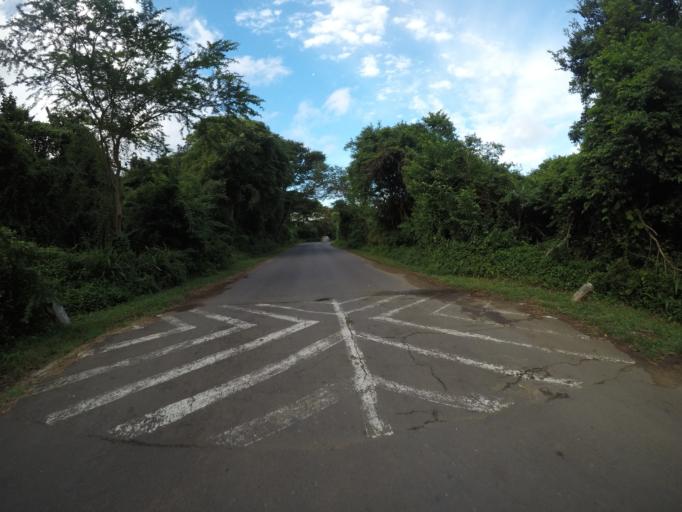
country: ZA
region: KwaZulu-Natal
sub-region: uMkhanyakude District Municipality
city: Mtubatuba
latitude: -28.3842
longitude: 32.4154
